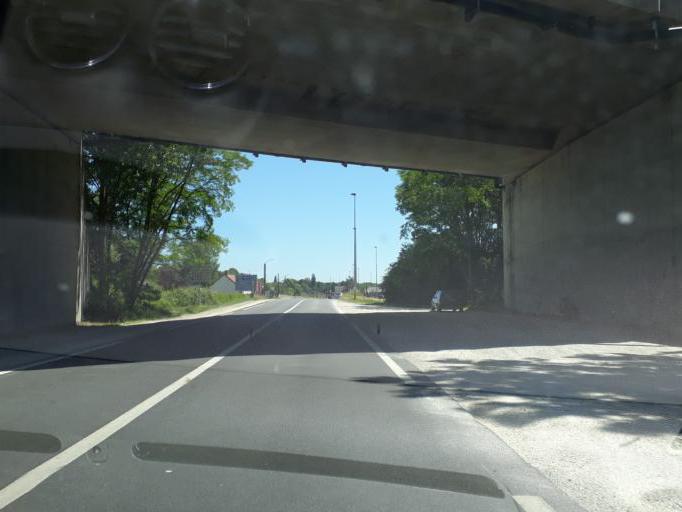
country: FR
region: Centre
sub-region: Departement du Cher
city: Vierzon
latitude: 47.2150
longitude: 2.1133
